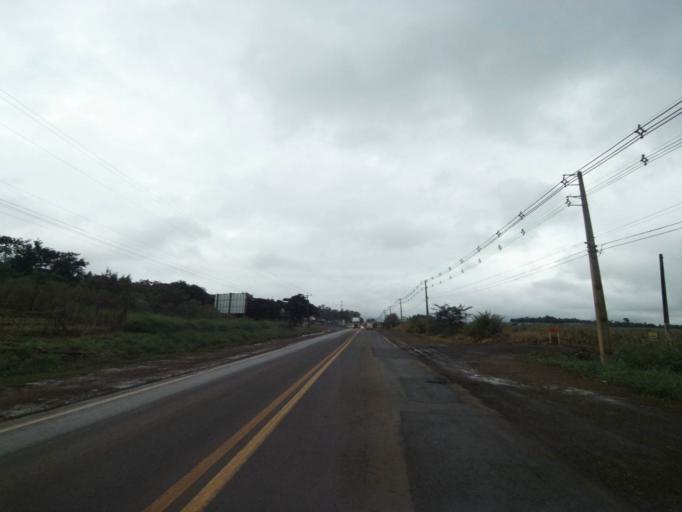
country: BR
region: Parana
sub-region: Marechal Candido Rondon
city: Marechal Candido Rondon
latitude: -24.5685
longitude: -54.0195
